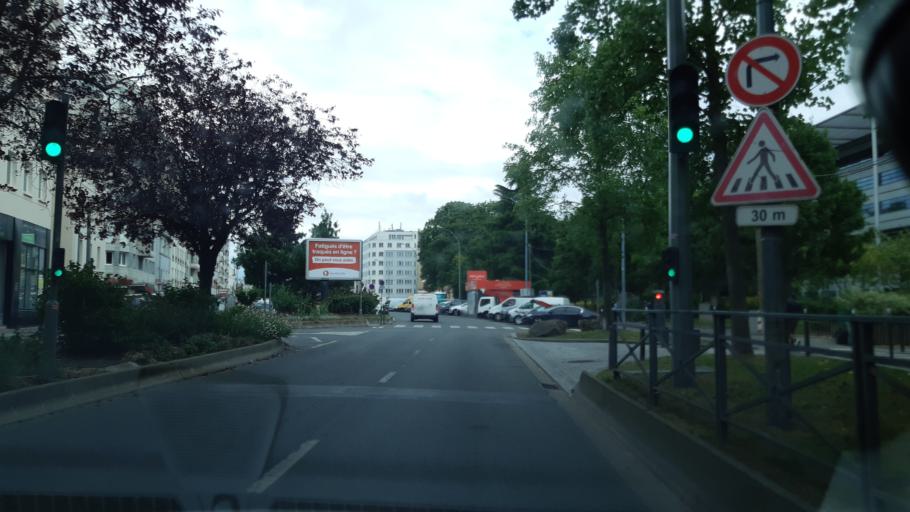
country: FR
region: Ile-de-France
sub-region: Paris
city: Saint-Ouen
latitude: 48.9147
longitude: 2.3318
